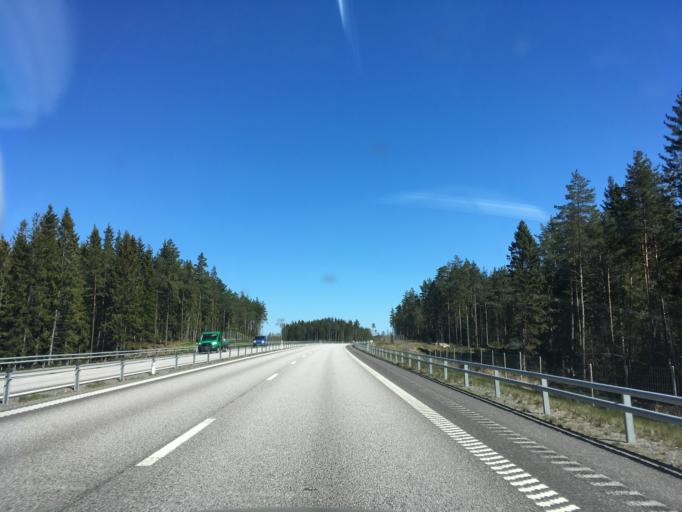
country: SE
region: Vaestra Goetaland
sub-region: Trollhattan
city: Sjuntorp
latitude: 58.2272
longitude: 12.2180
